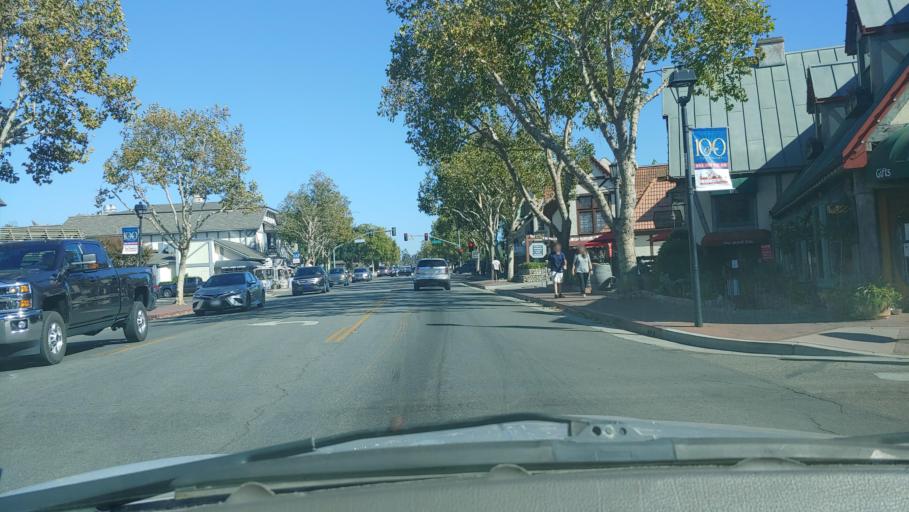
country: US
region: California
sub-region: Santa Barbara County
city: Solvang
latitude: 34.5960
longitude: -120.1394
